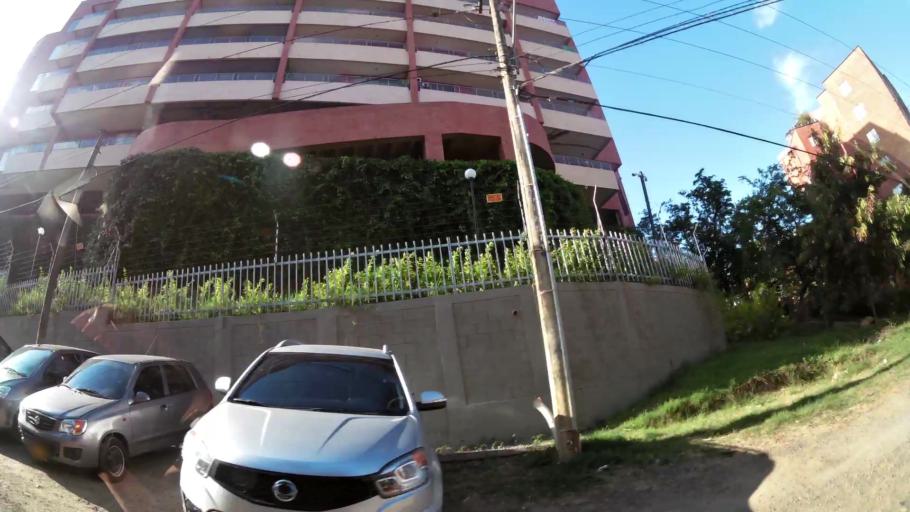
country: CO
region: Valle del Cauca
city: Cali
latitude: 3.4281
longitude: -76.5496
